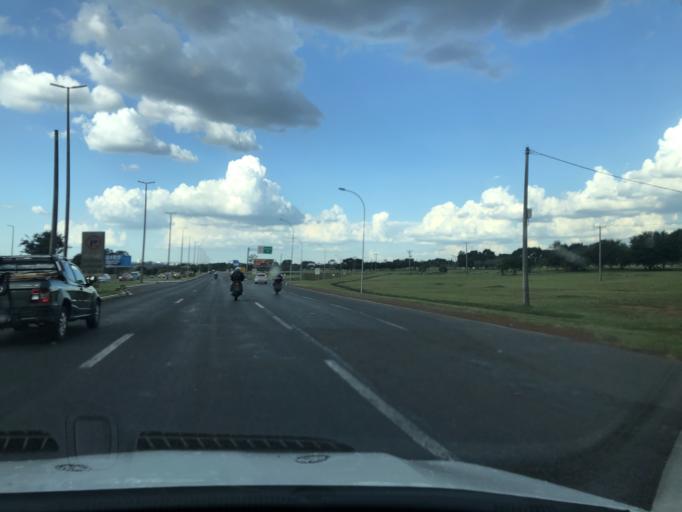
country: BR
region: Federal District
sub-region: Brasilia
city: Brasilia
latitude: -15.8653
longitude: -47.9407
